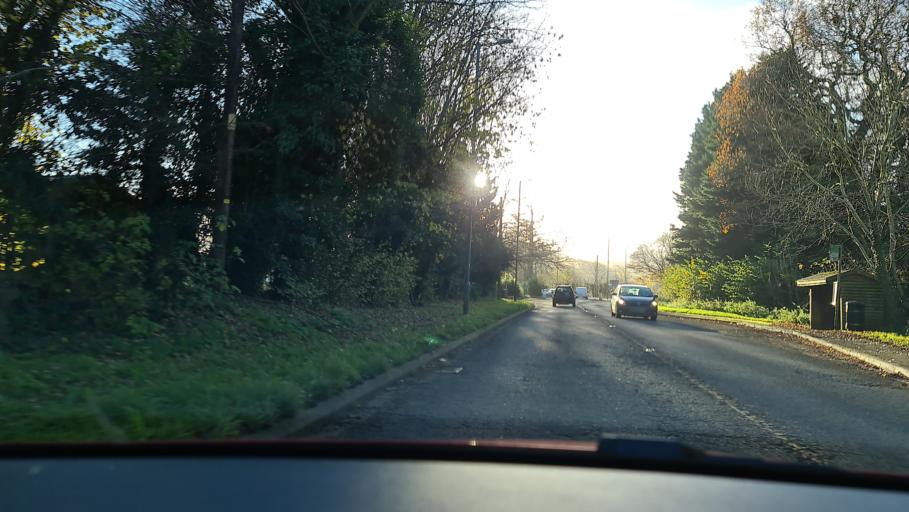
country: GB
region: England
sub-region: Buckinghamshire
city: Weston Turville
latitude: 51.7671
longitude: -0.7860
